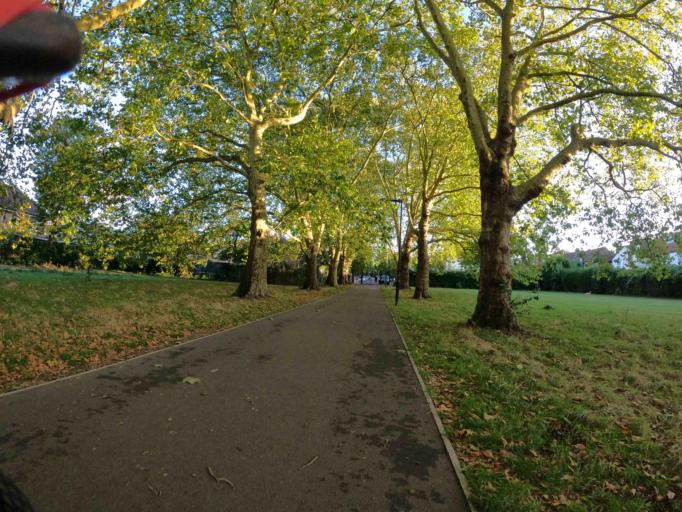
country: GB
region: England
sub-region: Greater London
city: Ealing Broadway
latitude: 51.5266
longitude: -0.3190
